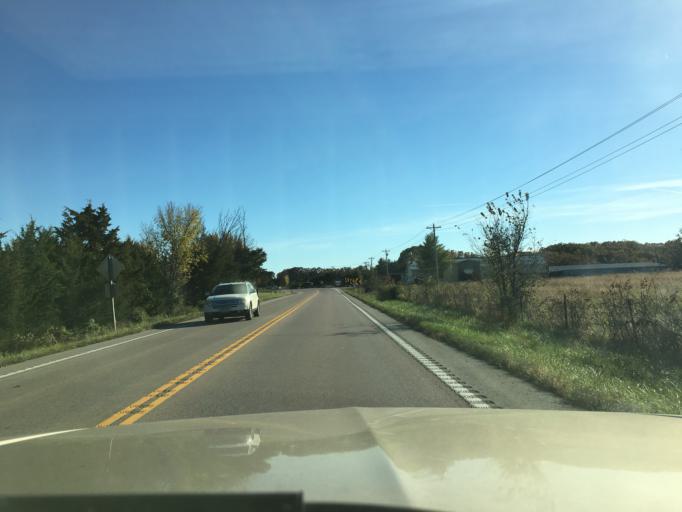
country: US
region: Missouri
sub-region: Gasconade County
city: Owensville
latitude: 38.4644
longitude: -91.4652
